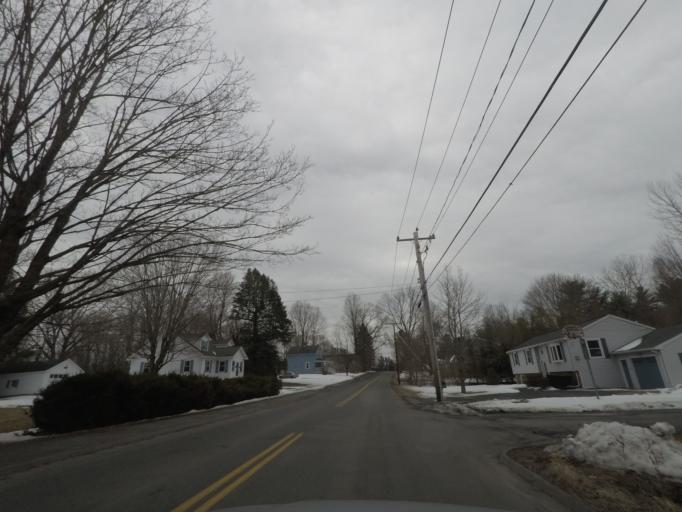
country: US
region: Massachusetts
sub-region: Berkshire County
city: Lee
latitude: 42.3092
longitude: -73.2565
